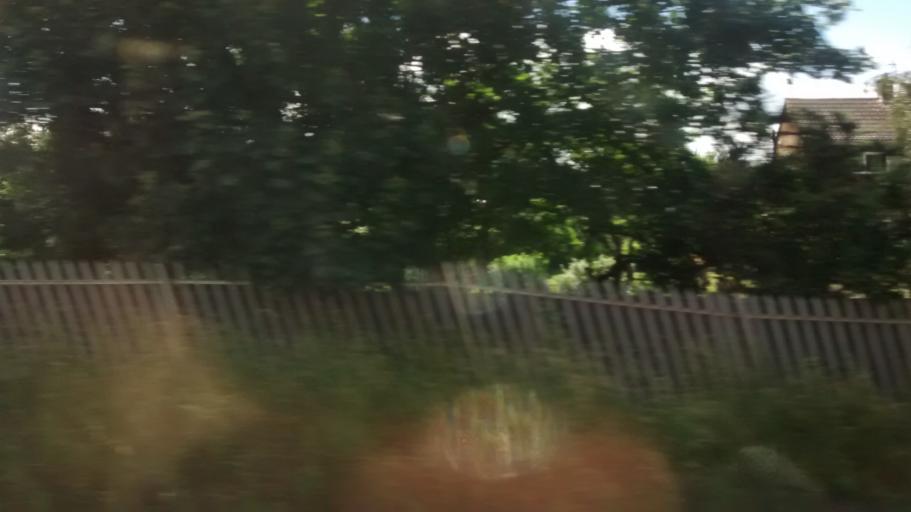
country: GB
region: England
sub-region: Nottinghamshire
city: Newark on Trent
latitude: 53.0629
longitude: -0.7780
